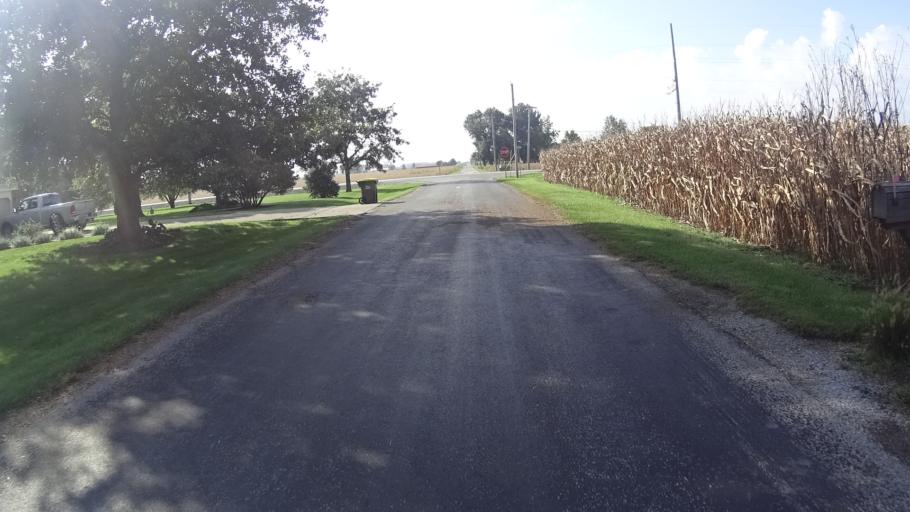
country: US
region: Indiana
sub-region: Madison County
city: Lapel
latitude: 40.0168
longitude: -85.8243
